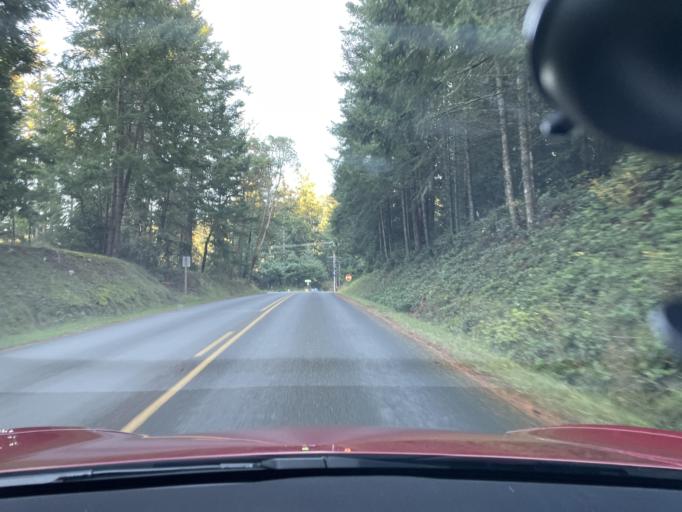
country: US
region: Washington
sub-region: San Juan County
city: Friday Harbor
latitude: 48.5615
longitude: -123.1422
